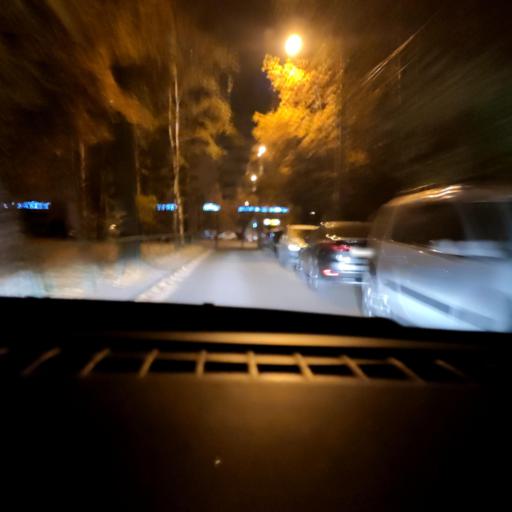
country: RU
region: Voronezj
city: Podgornoye
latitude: 51.7109
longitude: 39.1547
